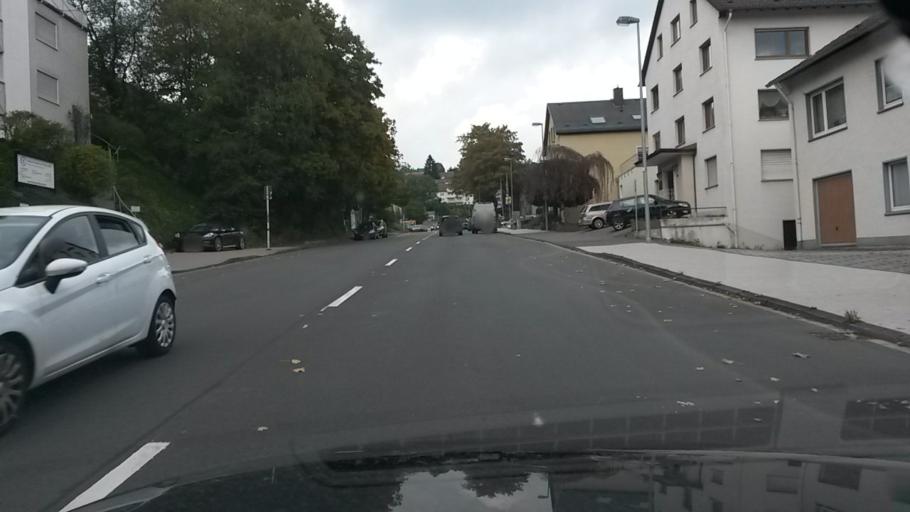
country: DE
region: North Rhine-Westphalia
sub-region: Regierungsbezirk Arnsberg
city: Luedenscheid
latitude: 51.2124
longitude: 7.6161
